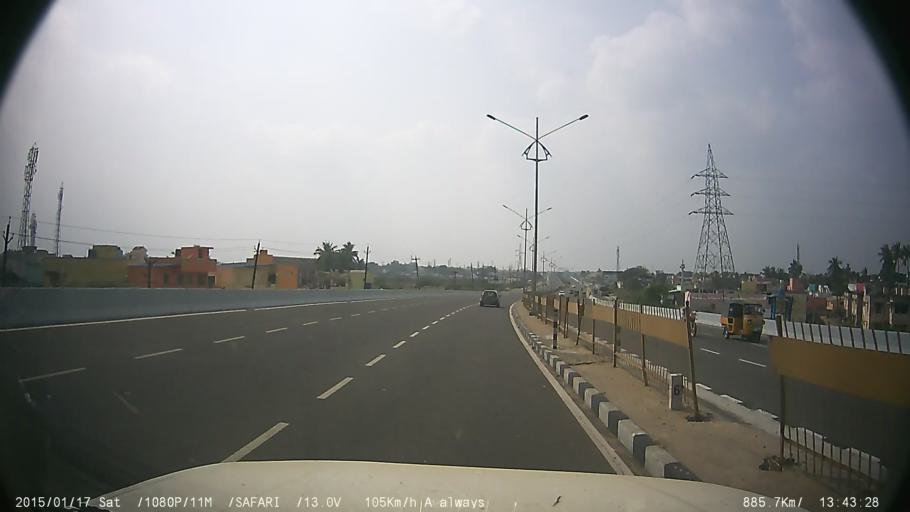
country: IN
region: Tamil Nadu
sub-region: Vellore
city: Vellore
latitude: 12.9269
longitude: 79.1236
